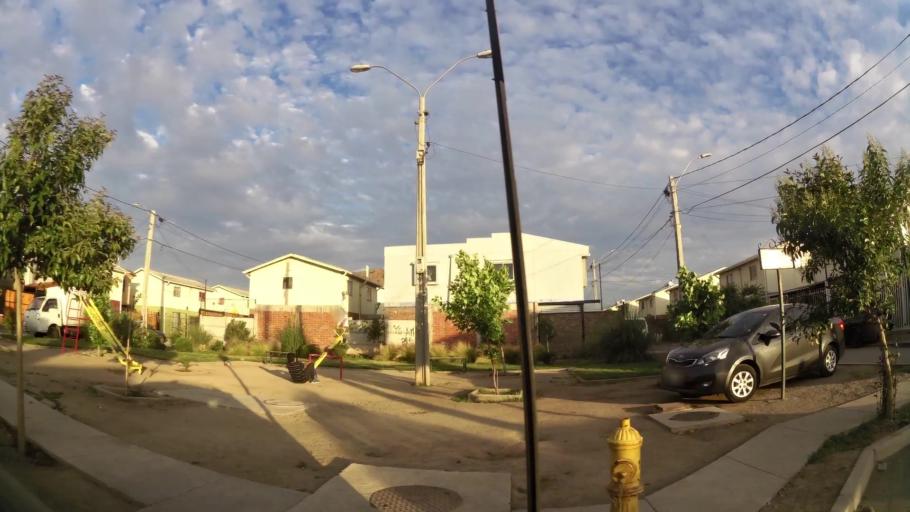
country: CL
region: Santiago Metropolitan
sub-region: Provincia de Maipo
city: San Bernardo
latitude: -33.6232
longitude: -70.6911
